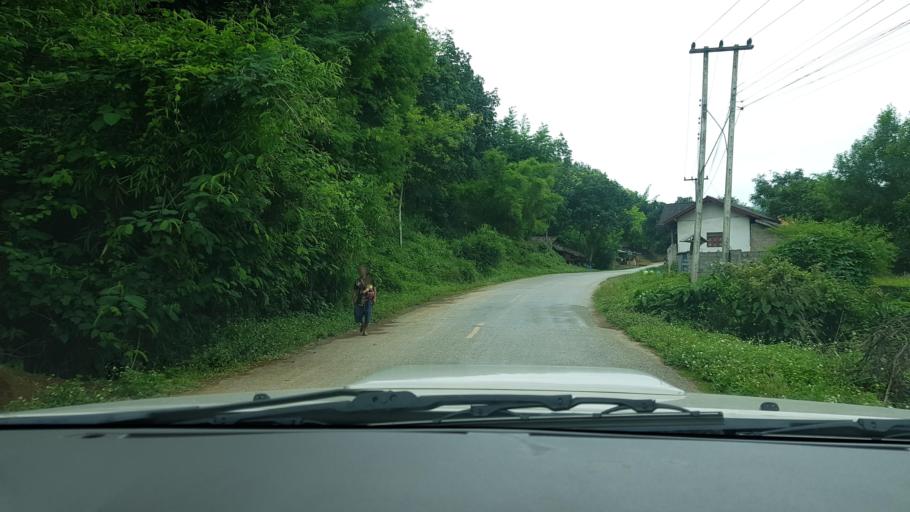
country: LA
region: Loungnamtha
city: Muang Nale
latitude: 20.2201
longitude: 101.5493
